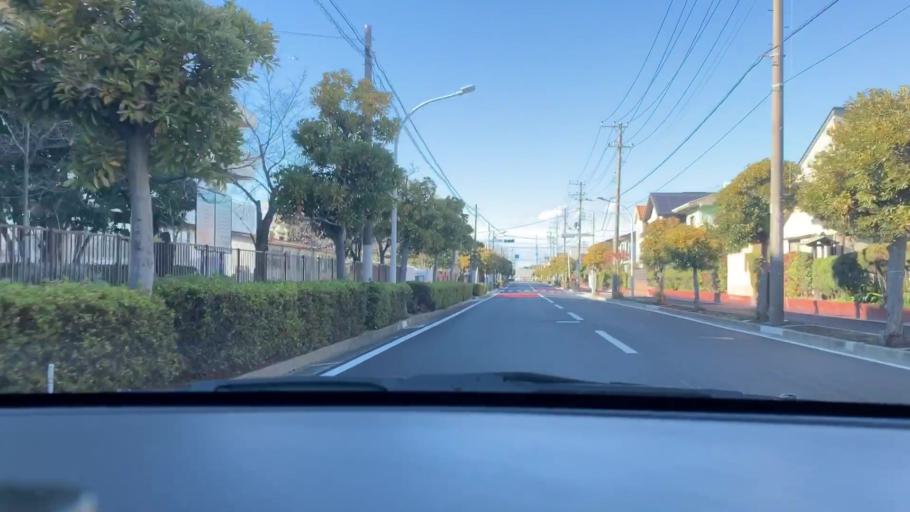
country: JP
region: Tokyo
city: Urayasu
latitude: 35.6384
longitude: 139.8973
